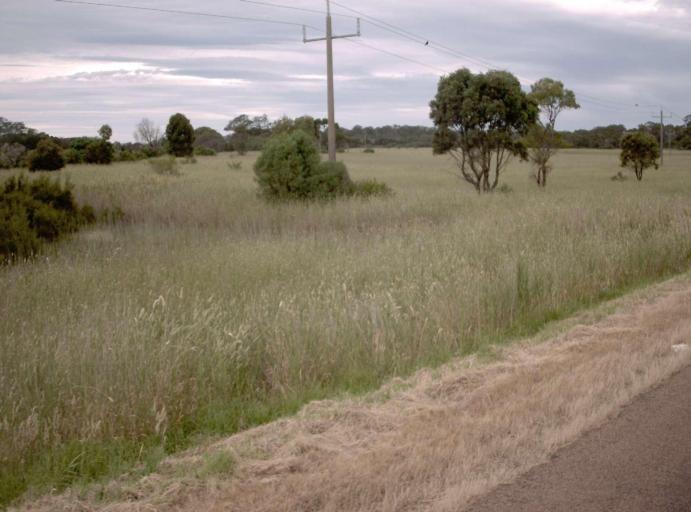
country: AU
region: Victoria
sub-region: East Gippsland
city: Bairnsdale
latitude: -37.8825
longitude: 147.6578
